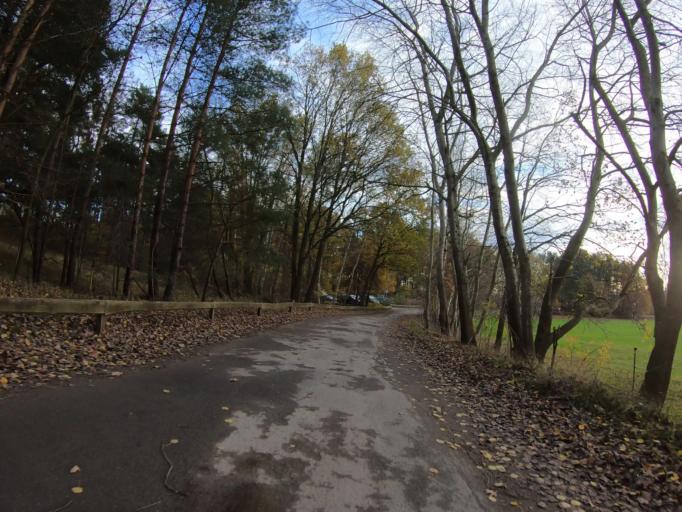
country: DE
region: Lower Saxony
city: Ribbesbuttel
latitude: 52.4667
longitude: 10.5057
